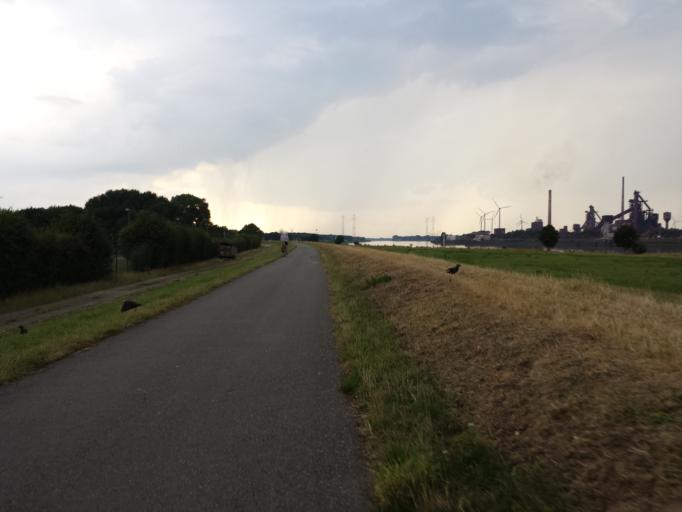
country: DE
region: Lower Saxony
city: Ritterhude
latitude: 53.1165
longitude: 8.7099
